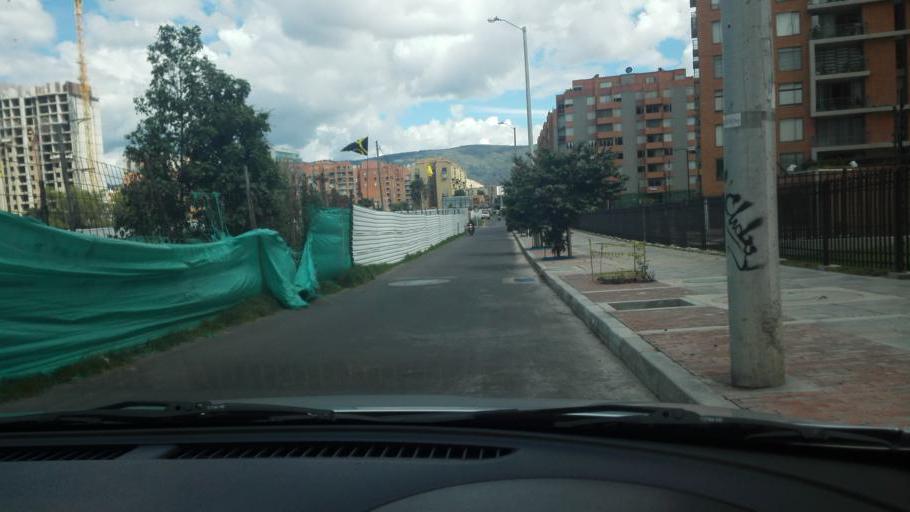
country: CO
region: Cundinamarca
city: Cota
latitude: 4.7412
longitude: -74.0697
